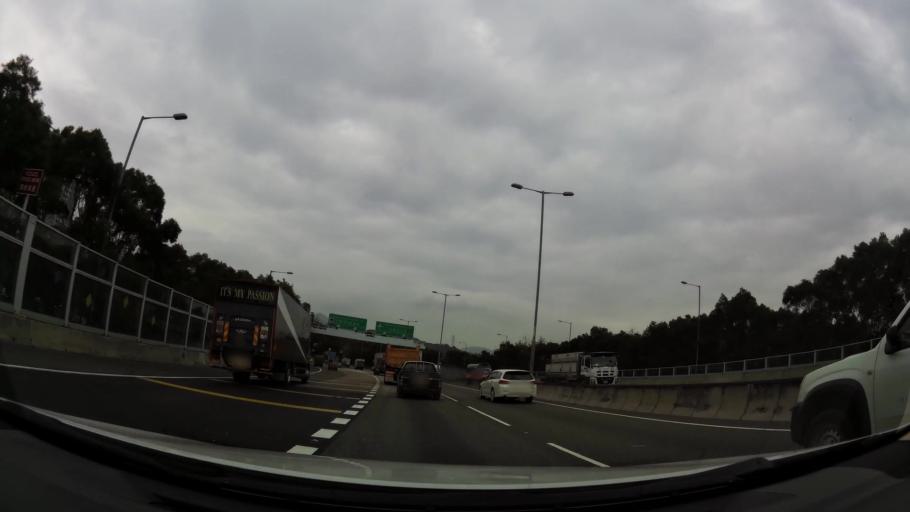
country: HK
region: Yuen Long
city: Yuen Long Kau Hui
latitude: 22.4343
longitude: 114.0327
